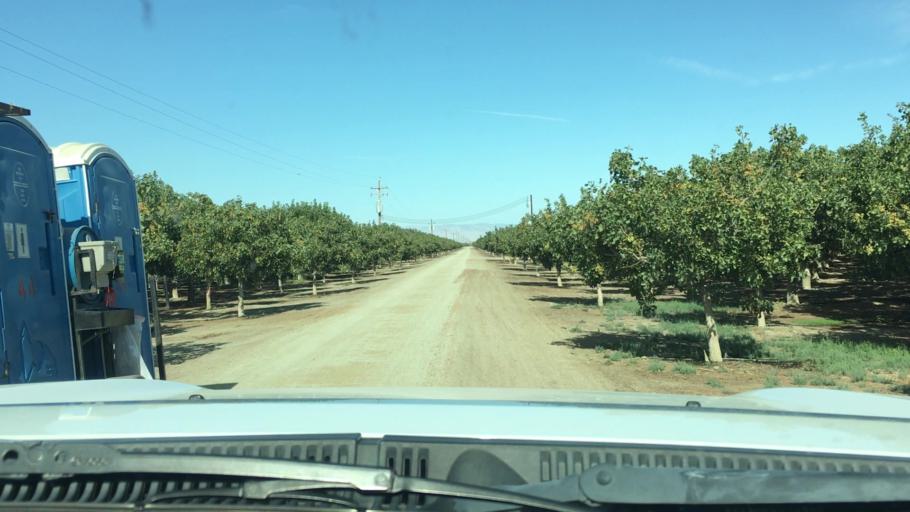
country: US
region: California
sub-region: Kern County
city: Buttonwillow
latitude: 35.3694
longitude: -119.3915
